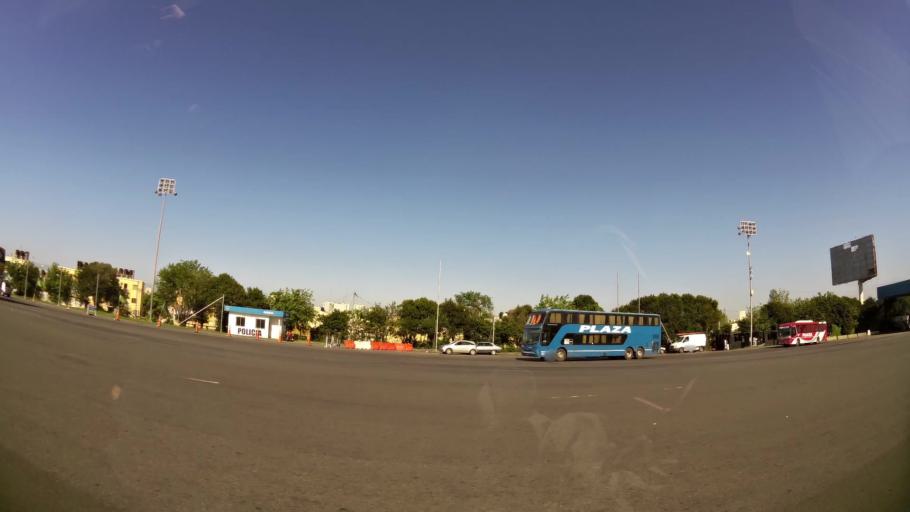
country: AR
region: Buenos Aires
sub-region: Partido de Avellaneda
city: Avellaneda
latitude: -34.6518
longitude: -58.3533
